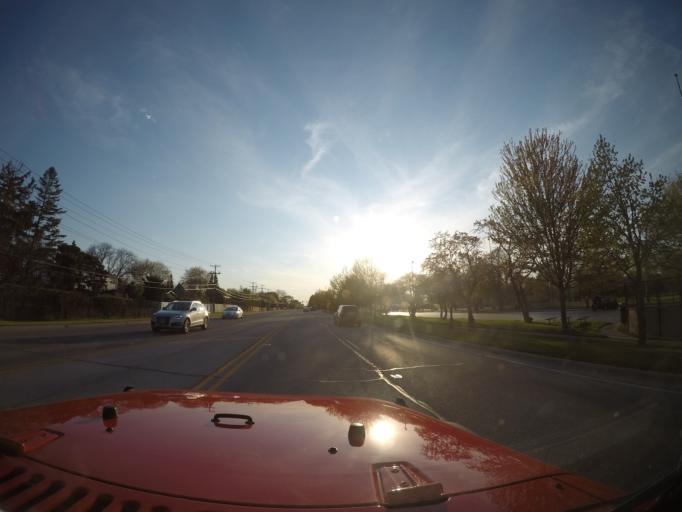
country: US
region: Illinois
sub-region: Cook County
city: Prospect Heights
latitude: 42.0879
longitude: -87.9099
